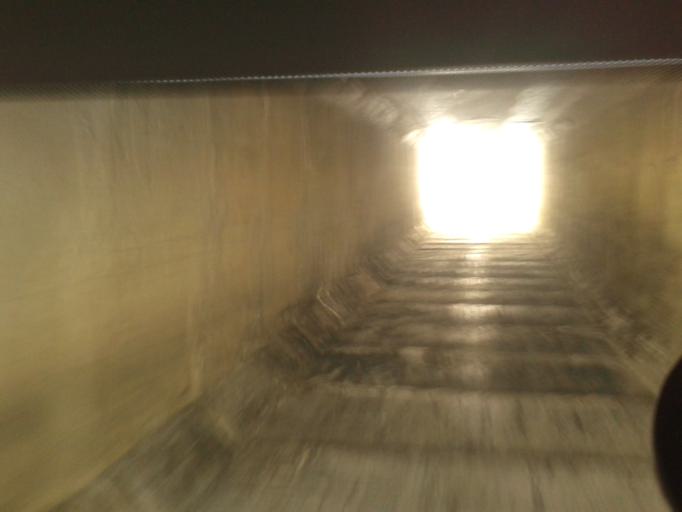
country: RU
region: Volgograd
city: Volgograd
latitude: 48.6306
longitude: 44.4363
